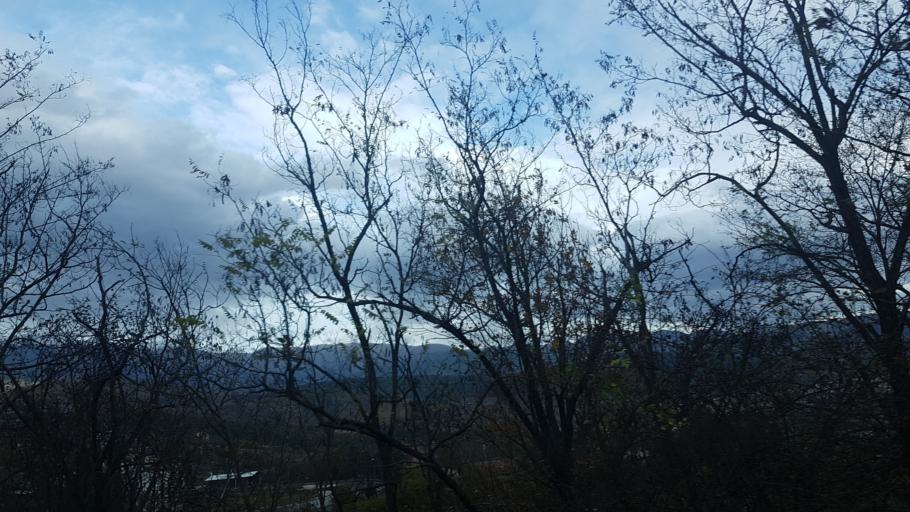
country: IT
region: Abruzzo
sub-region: Provincia dell' Aquila
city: Progetto Case Bazzano
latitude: 42.3629
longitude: 13.4290
